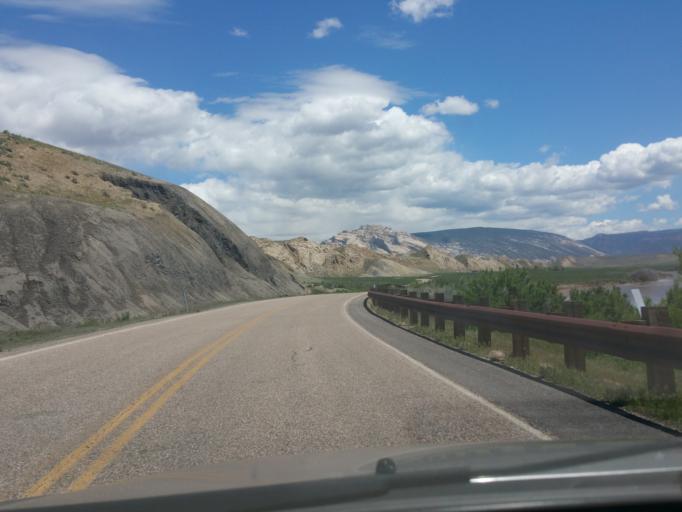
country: US
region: Utah
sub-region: Uintah County
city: Naples
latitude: 40.4371
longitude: -109.3276
